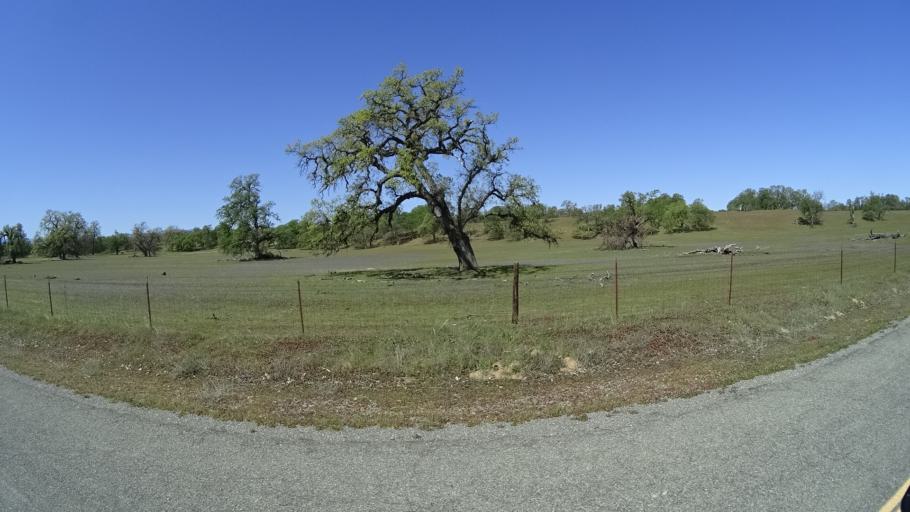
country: US
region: California
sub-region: Glenn County
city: Orland
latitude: 39.7420
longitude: -122.4041
